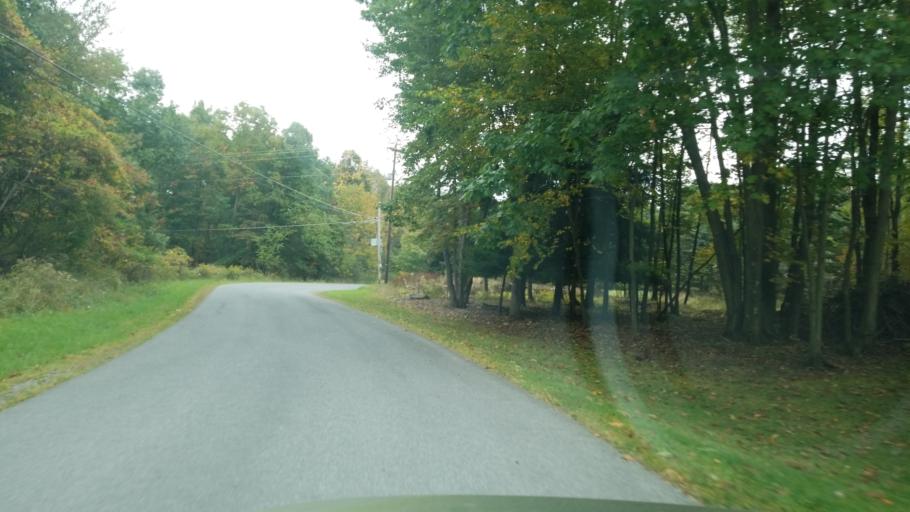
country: US
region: Pennsylvania
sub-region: Clearfield County
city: Curwensville
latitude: 41.0090
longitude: -78.5387
